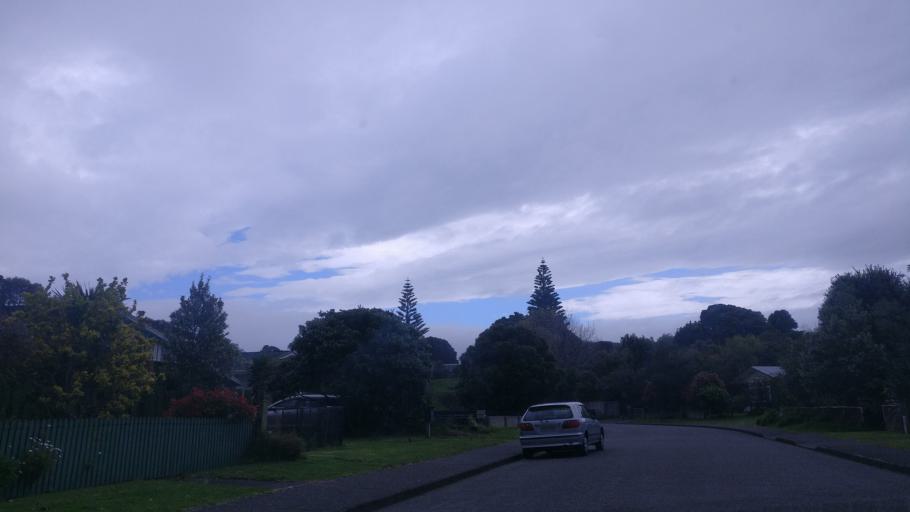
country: NZ
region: Wellington
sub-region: Kapiti Coast District
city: Paraparaumu
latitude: -40.9814
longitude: 174.9593
